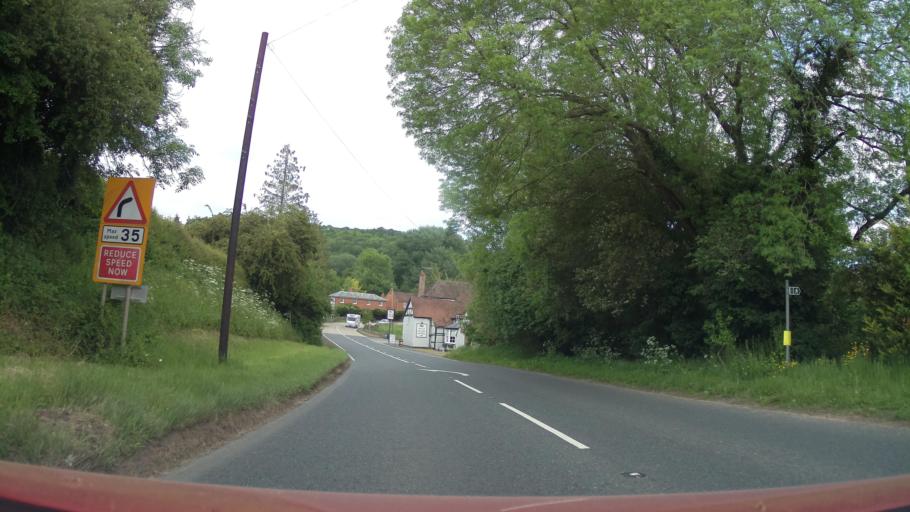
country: GB
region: England
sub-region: Herefordshire
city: Evesbatch
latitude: 52.1295
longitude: -2.3912
